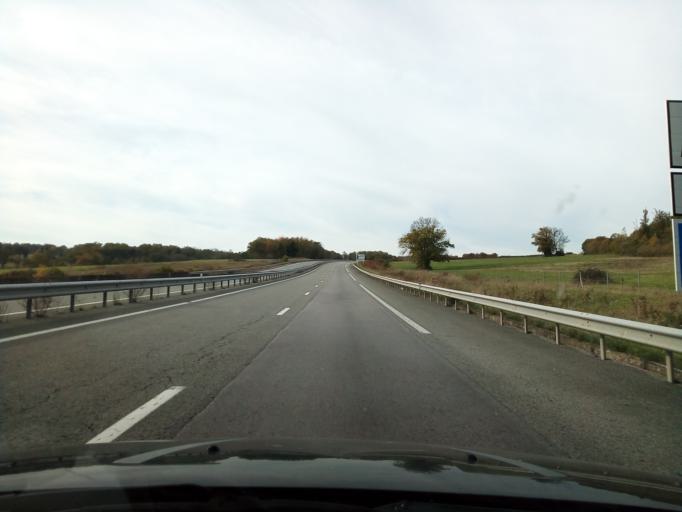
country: FR
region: Limousin
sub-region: Departement de la Creuse
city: Ajain
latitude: 46.2017
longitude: 2.1066
